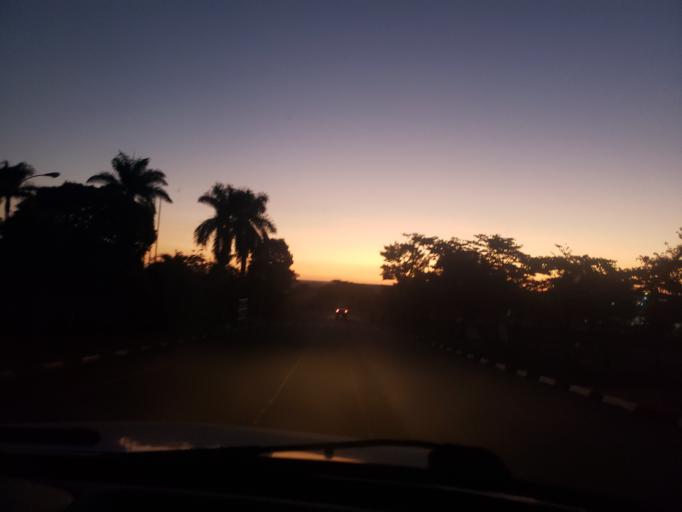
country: BR
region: Sao Paulo
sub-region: Conchal
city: Conchal
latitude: -22.2916
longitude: -47.1336
